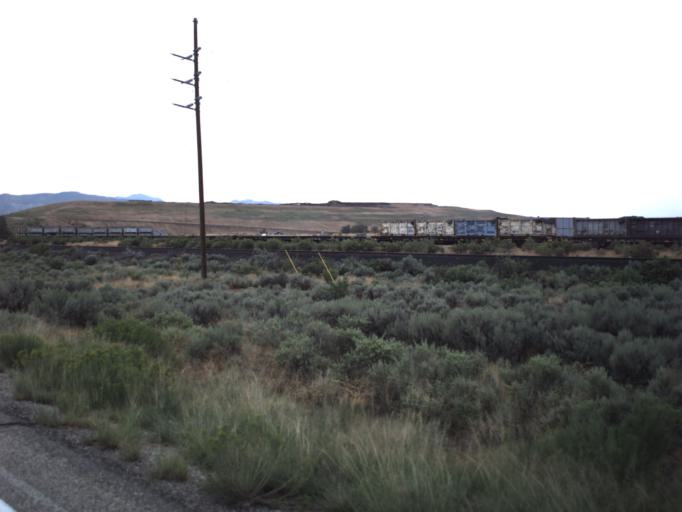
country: US
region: Utah
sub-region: Carbon County
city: East Carbon City
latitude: 39.5357
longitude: -110.4879
